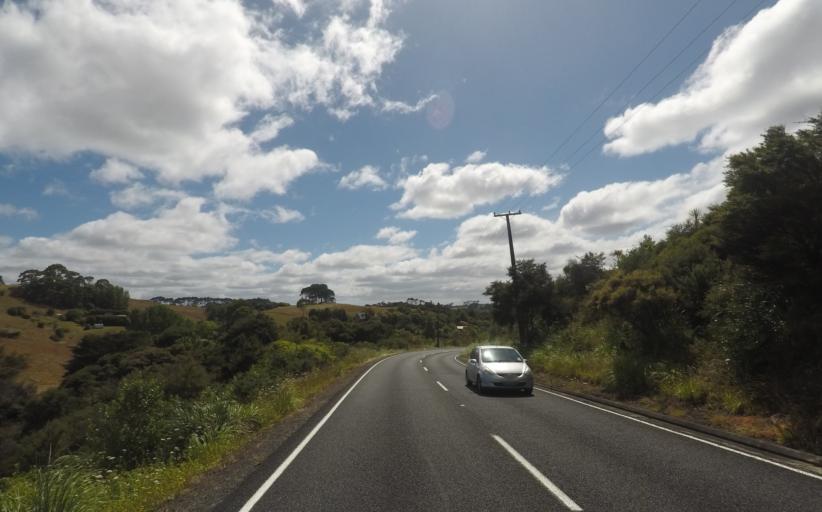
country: NZ
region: Auckland
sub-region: Auckland
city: Muriwai Beach
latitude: -36.8519
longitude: 174.5326
